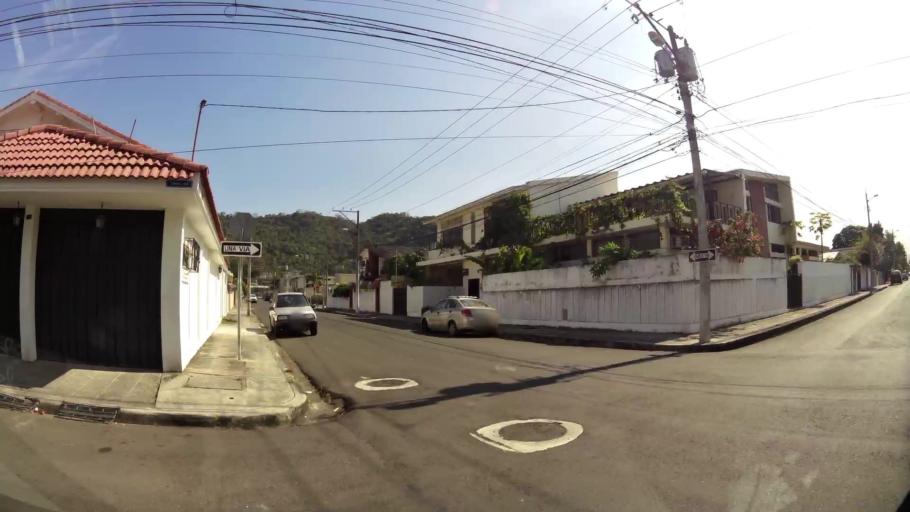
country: EC
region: Guayas
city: Guayaquil
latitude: -2.1662
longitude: -79.9182
